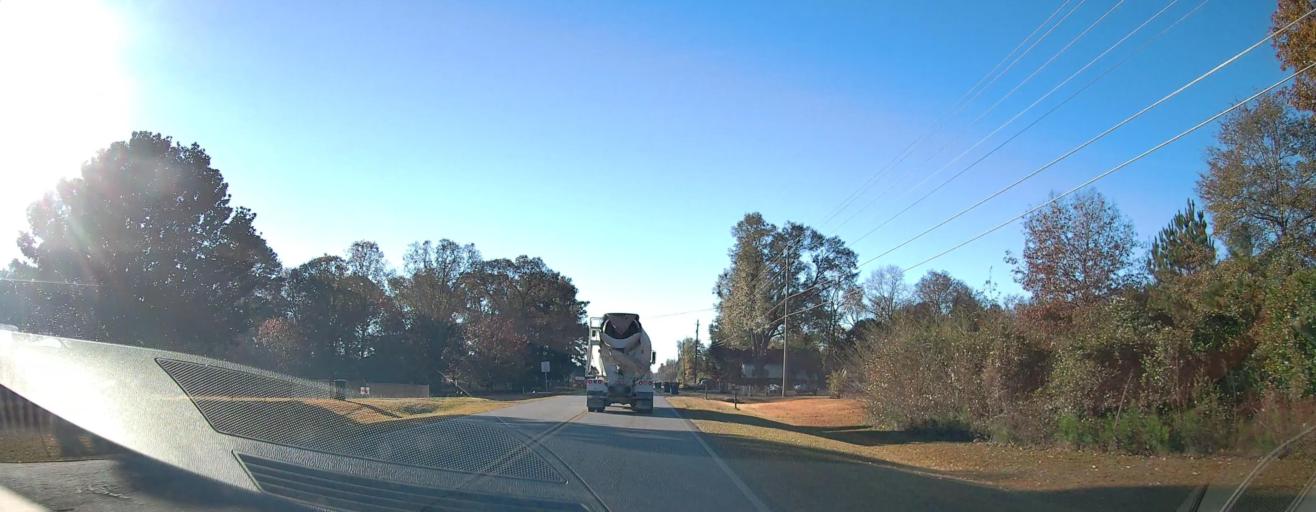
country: US
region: Georgia
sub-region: Houston County
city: Centerville
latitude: 32.5573
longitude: -83.7197
